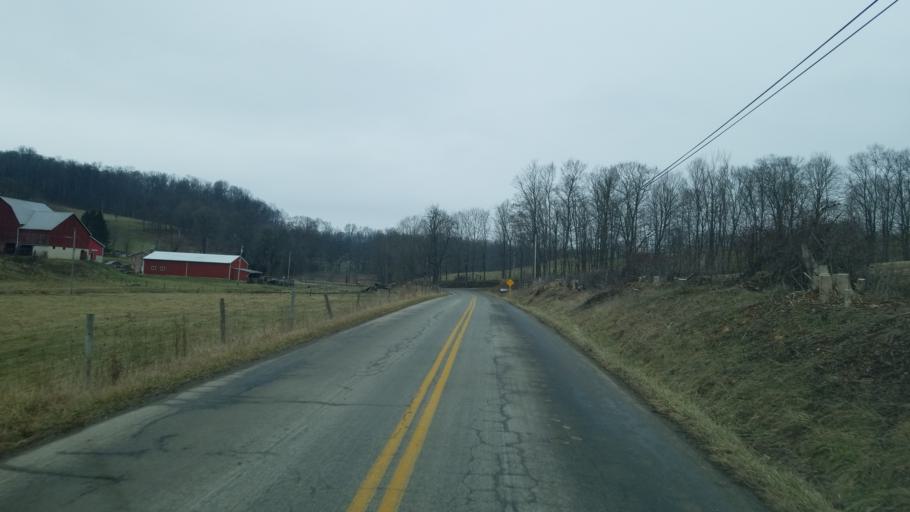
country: US
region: Ohio
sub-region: Holmes County
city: Millersburg
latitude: 40.4977
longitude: -81.8819
